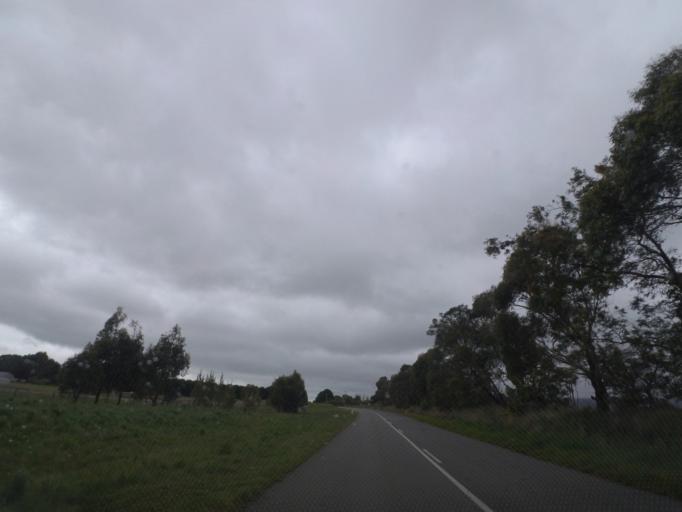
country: AU
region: Victoria
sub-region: Hume
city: Sunbury
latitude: -37.3230
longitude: 144.5453
